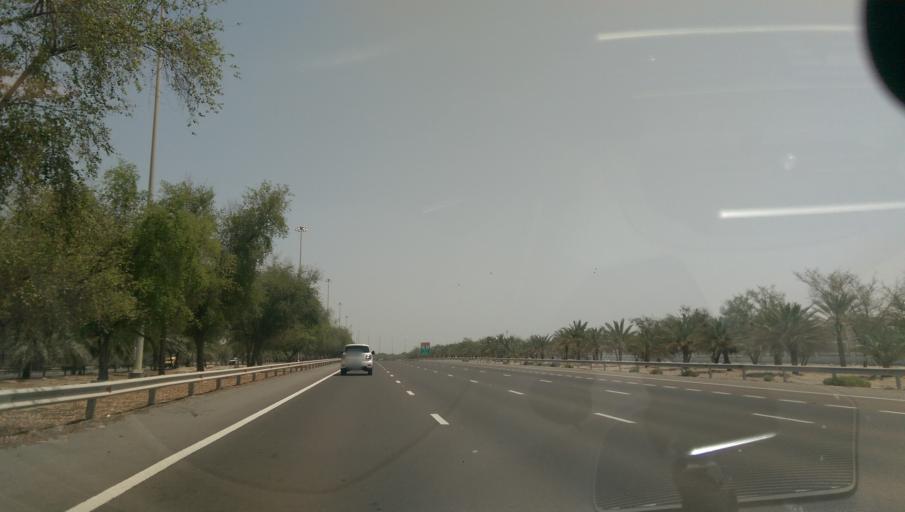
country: AE
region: Abu Dhabi
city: Abu Dhabi
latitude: 24.4757
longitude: 54.6760
